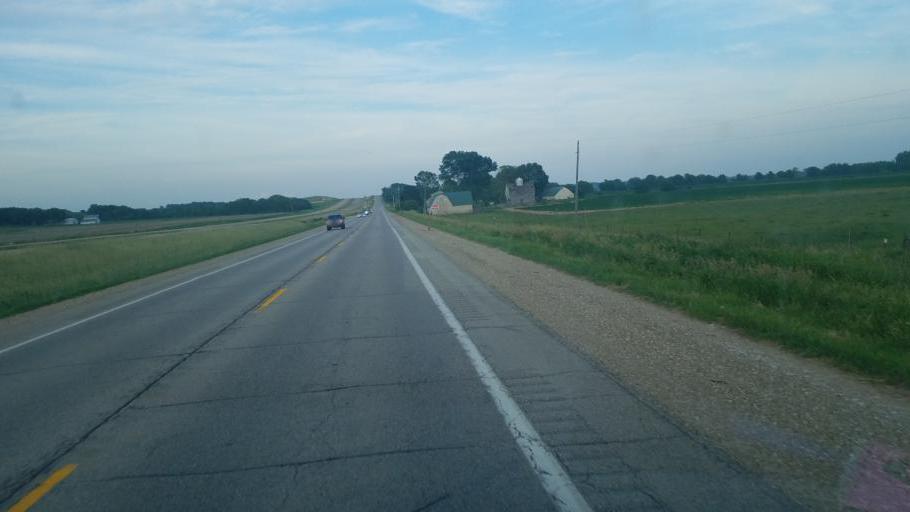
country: US
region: Iowa
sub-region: Tama County
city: Tama
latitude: 41.9638
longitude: -92.4693
